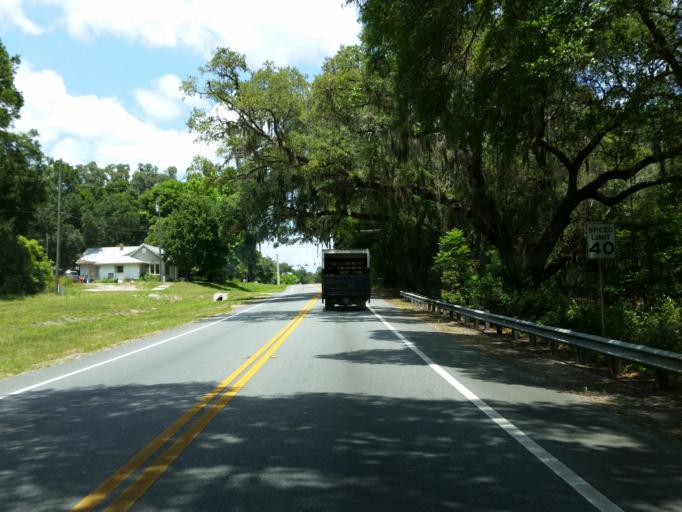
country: US
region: Florida
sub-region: Marion County
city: Belleview
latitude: 29.0068
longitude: -82.0413
